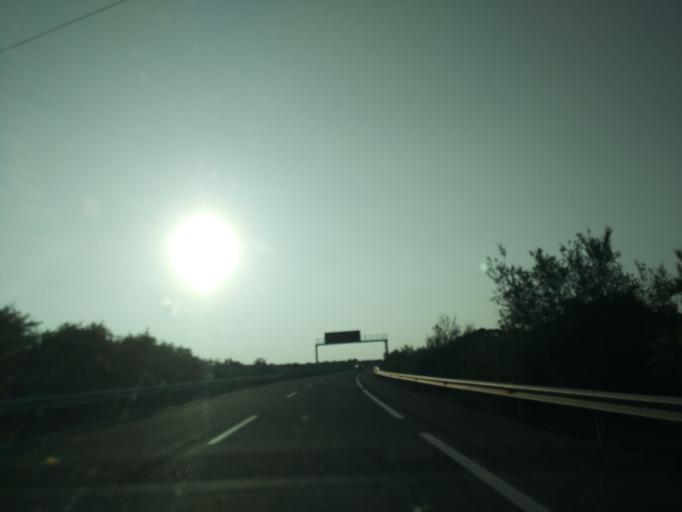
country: ES
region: Castille and Leon
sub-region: Provincia de Avila
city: Berrocalejo de Aragona
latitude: 40.6749
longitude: -4.6202
